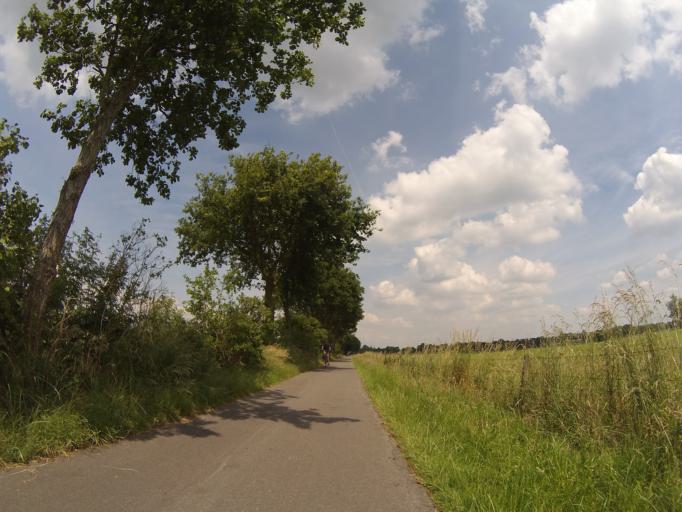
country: NL
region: Utrecht
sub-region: Gemeente De Bilt
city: De Bilt
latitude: 52.1477
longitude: 5.1675
